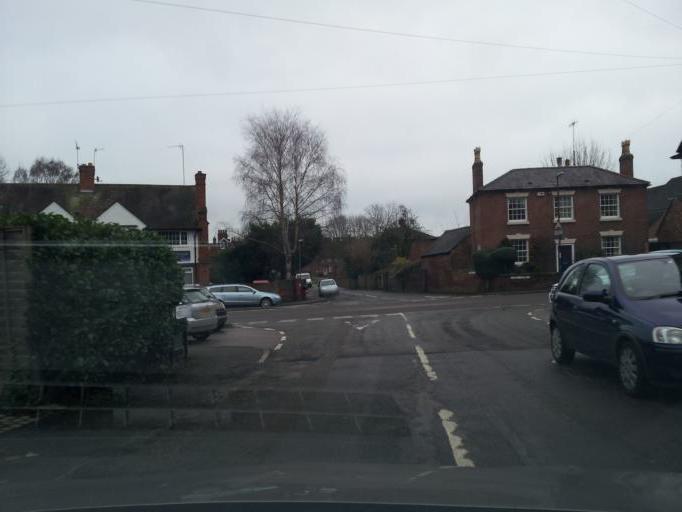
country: GB
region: England
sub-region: Derbyshire
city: Repton
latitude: 52.8353
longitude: -1.5464
